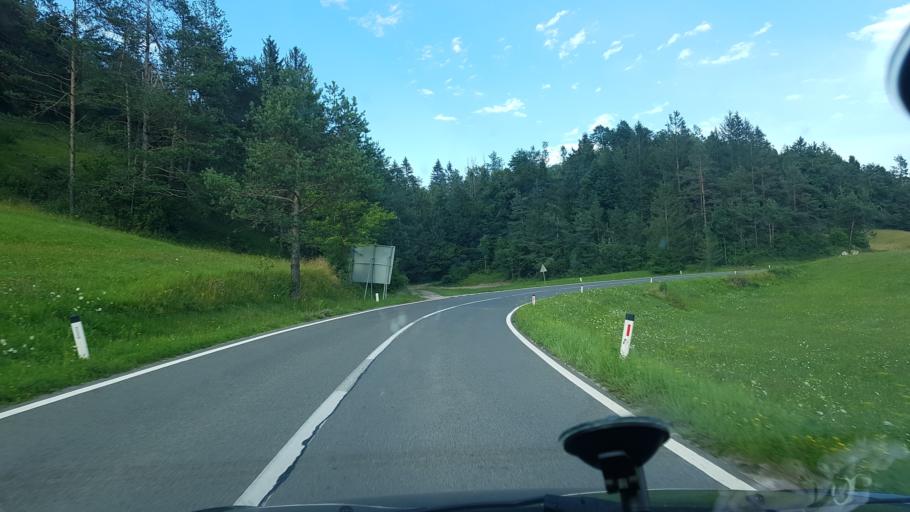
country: SI
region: Idrija
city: Idrija
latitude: 45.9552
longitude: 14.0971
